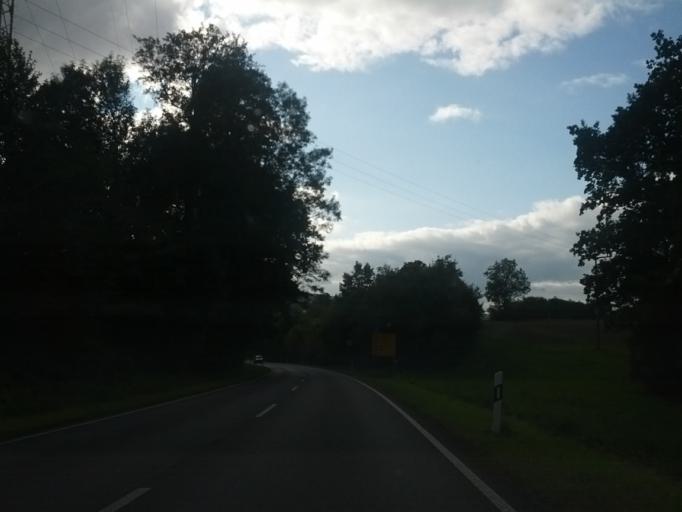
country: DE
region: Thuringia
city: Krauthausen
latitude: 51.0180
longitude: 10.2428
